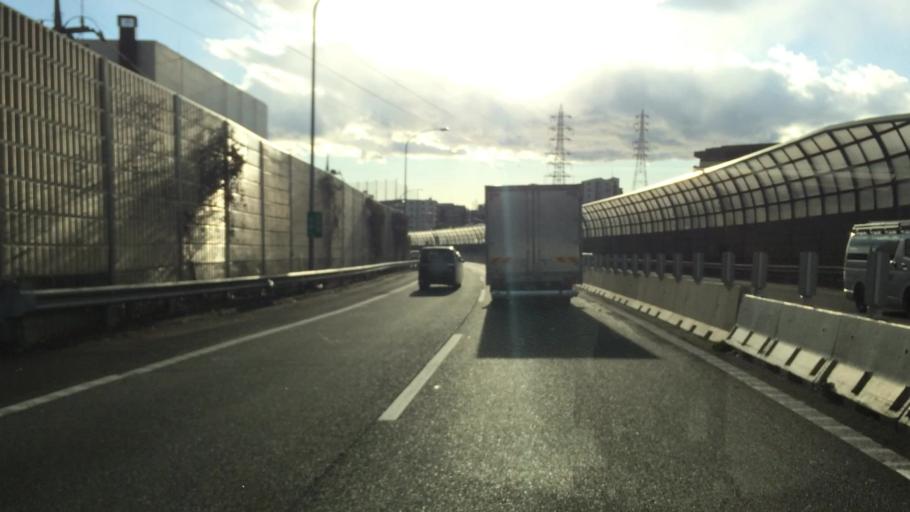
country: JP
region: Kanagawa
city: Yokohama
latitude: 35.4259
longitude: 139.5419
